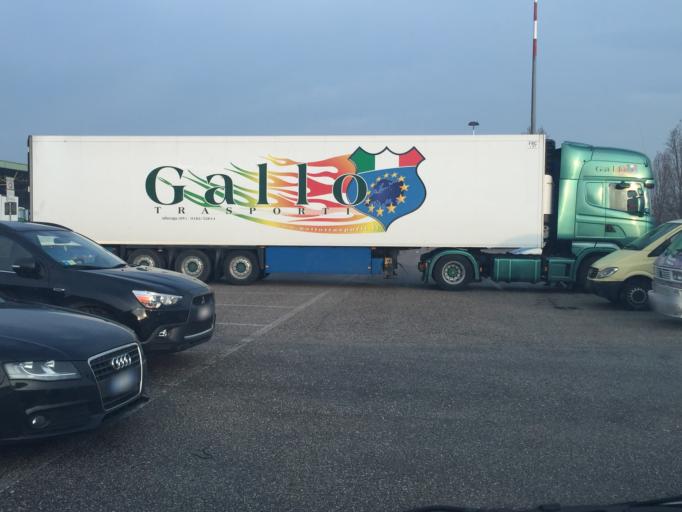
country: IT
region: Veneto
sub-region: Provincia di Verona
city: Dossobuono
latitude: 45.4103
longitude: 10.9231
